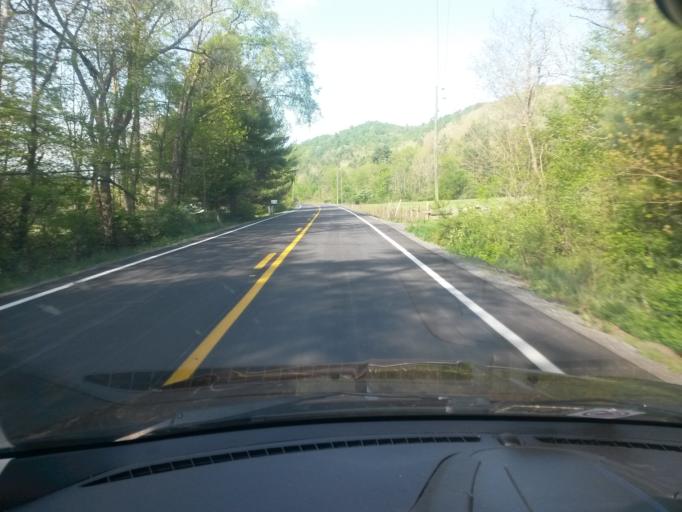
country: US
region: West Virginia
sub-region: Pocahontas County
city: Marlinton
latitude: 38.0217
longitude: -80.0459
